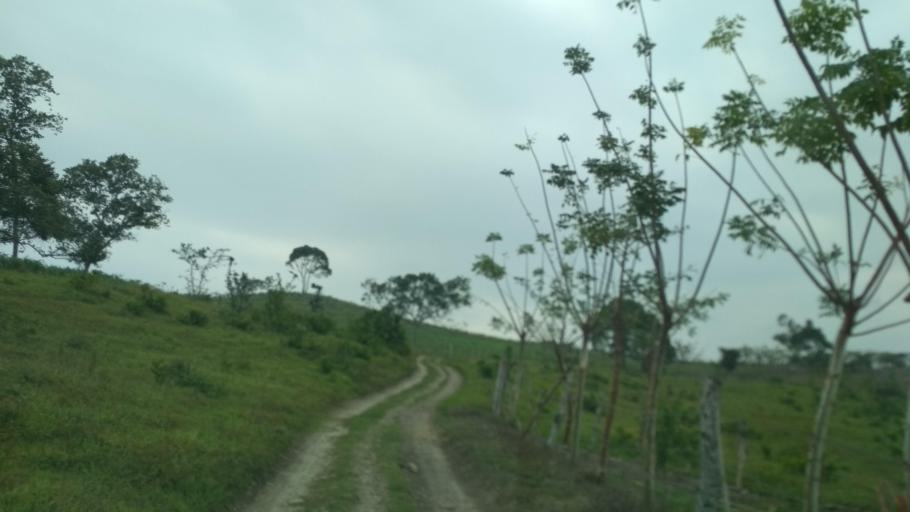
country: MM
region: Kayah
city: Loikaw
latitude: 20.2095
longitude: 97.3268
